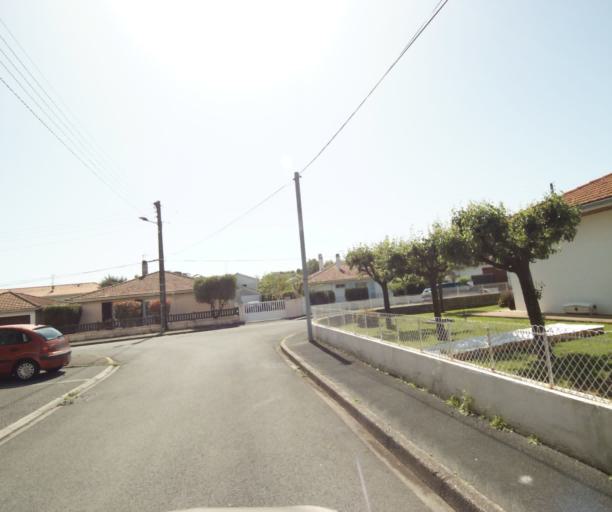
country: FR
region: Aquitaine
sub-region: Departement des Pyrenees-Atlantiques
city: Bayonne
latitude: 43.4766
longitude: -1.4629
